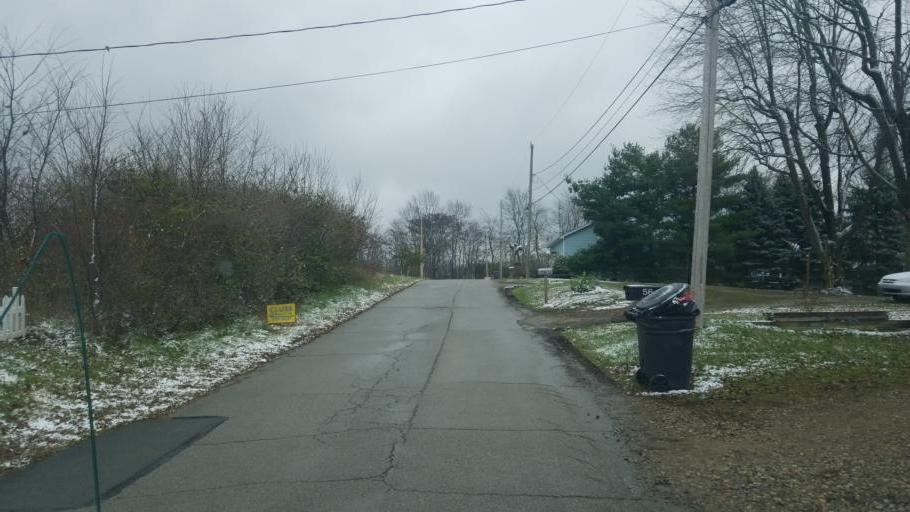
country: US
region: Ohio
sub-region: Richland County
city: Shelby
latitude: 40.8945
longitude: -82.6525
